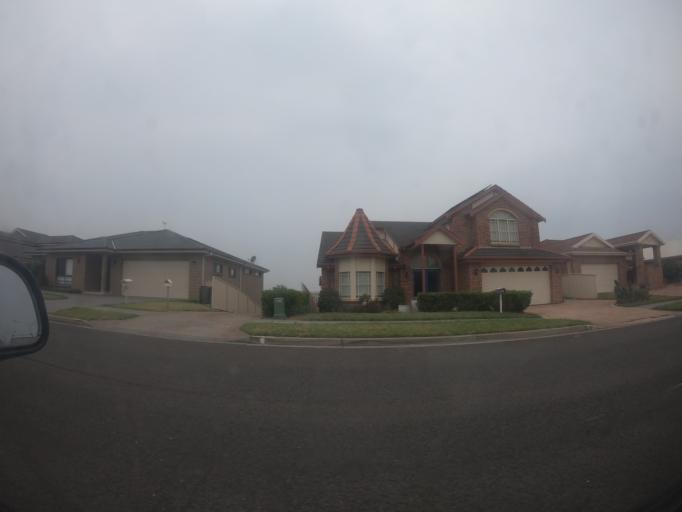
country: AU
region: New South Wales
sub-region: Shellharbour
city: Flinders
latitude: -34.5765
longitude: 150.8420
